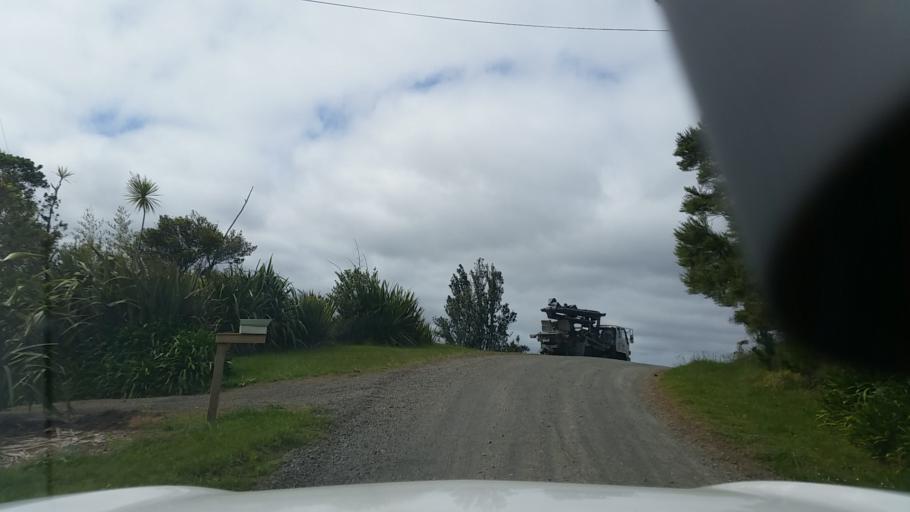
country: NZ
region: Auckland
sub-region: Auckland
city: Muriwai Beach
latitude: -36.8420
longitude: 174.5124
